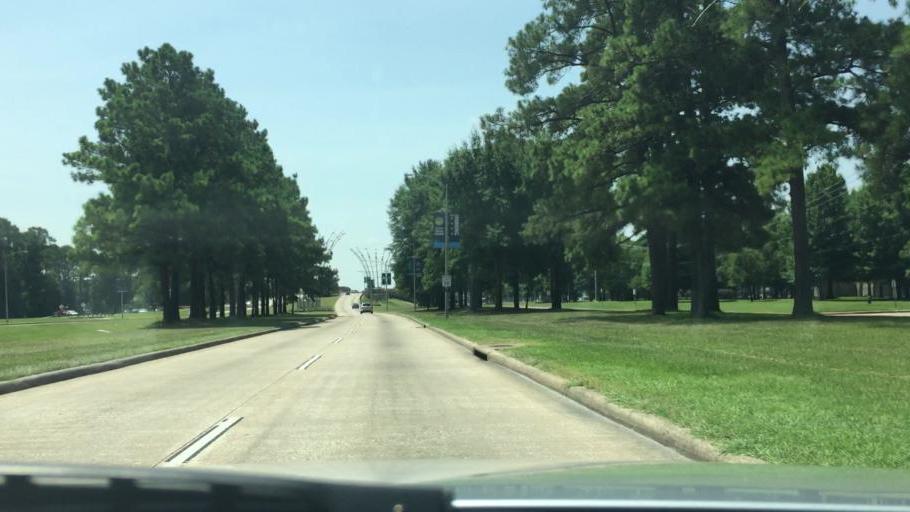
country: US
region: Texas
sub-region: Harris County
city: Aldine
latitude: 29.9691
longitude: -95.3386
